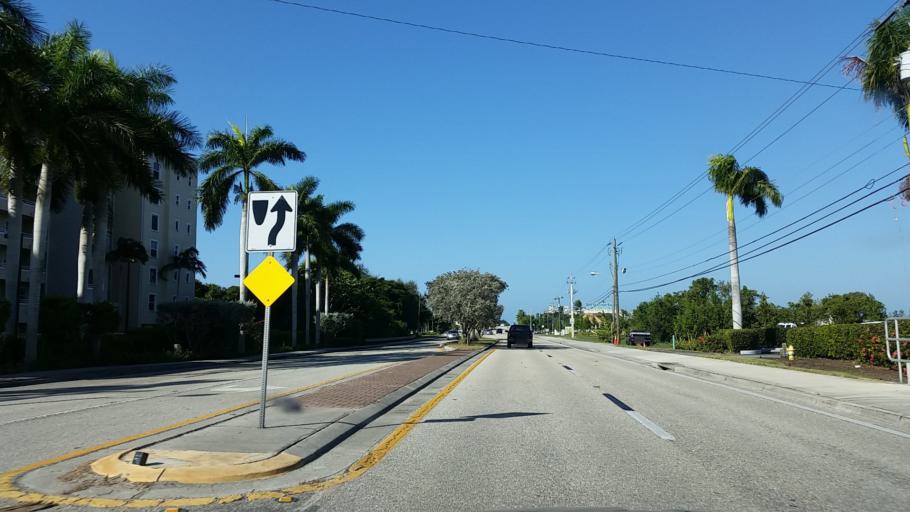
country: US
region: Florida
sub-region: Lee County
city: Bonita Springs
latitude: 26.3305
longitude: -81.8330
